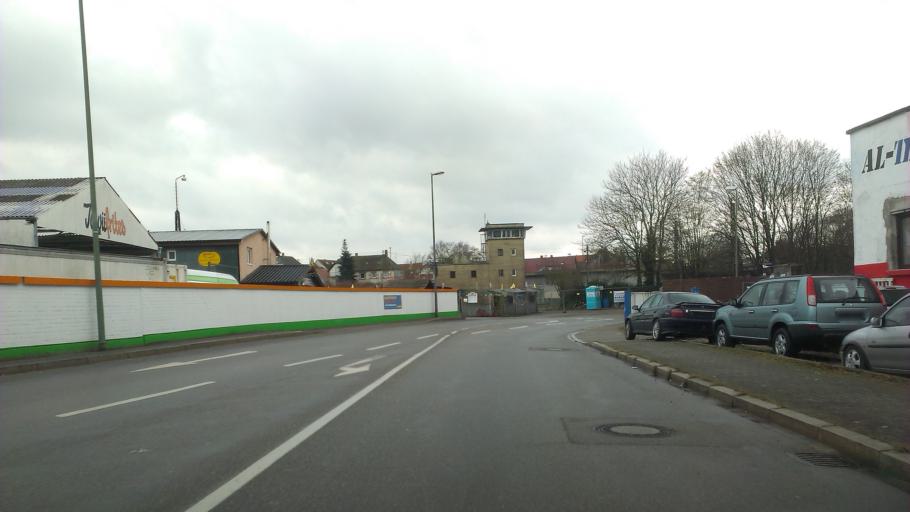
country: DE
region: Rheinland-Pfalz
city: Gartenstadt
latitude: 49.4951
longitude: 8.3791
